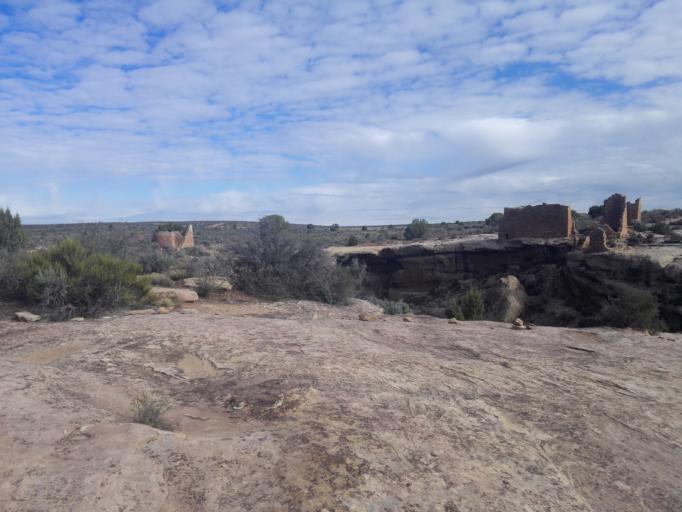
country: US
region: Colorado
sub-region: Montezuma County
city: Towaoc
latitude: 37.3851
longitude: -109.0808
